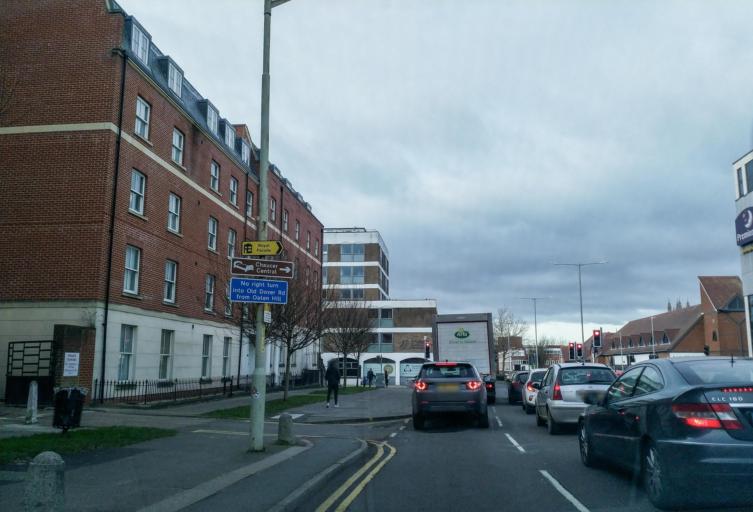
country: GB
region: England
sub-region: Kent
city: Canterbury
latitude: 51.2751
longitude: 1.0872
